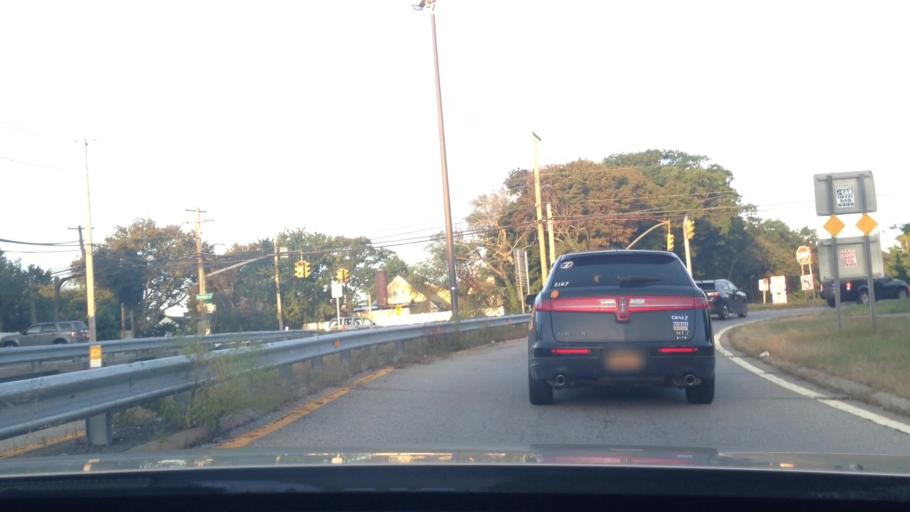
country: US
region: New York
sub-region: Nassau County
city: Lakeview
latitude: 40.6818
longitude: -73.6629
